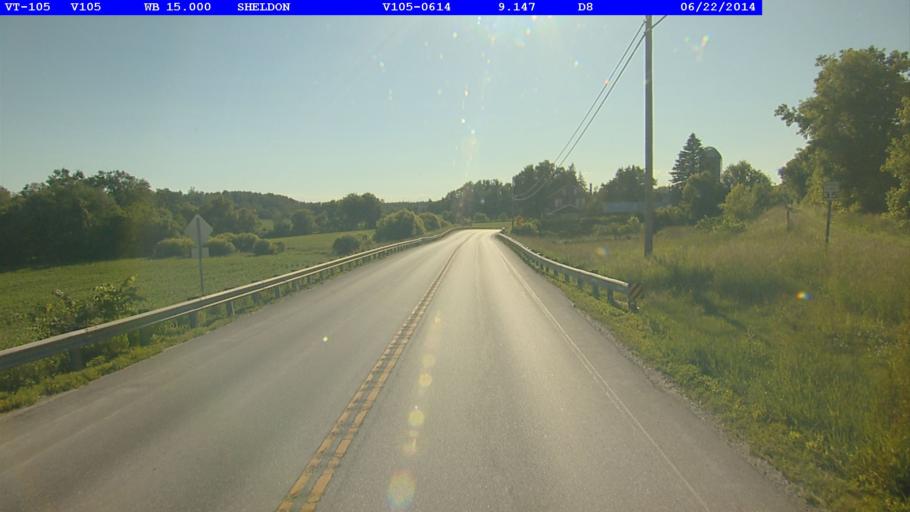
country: US
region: Vermont
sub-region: Franklin County
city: Enosburg Falls
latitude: 44.9089
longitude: -72.8575
